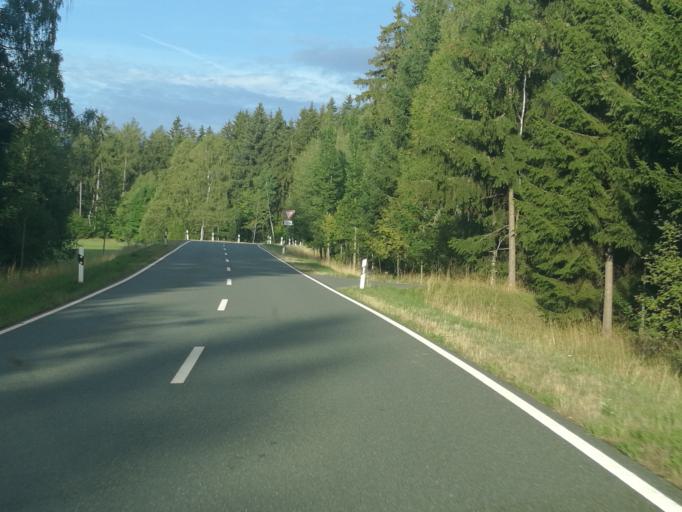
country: DE
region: Saxony
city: Eichigt
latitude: 50.3358
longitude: 12.1658
